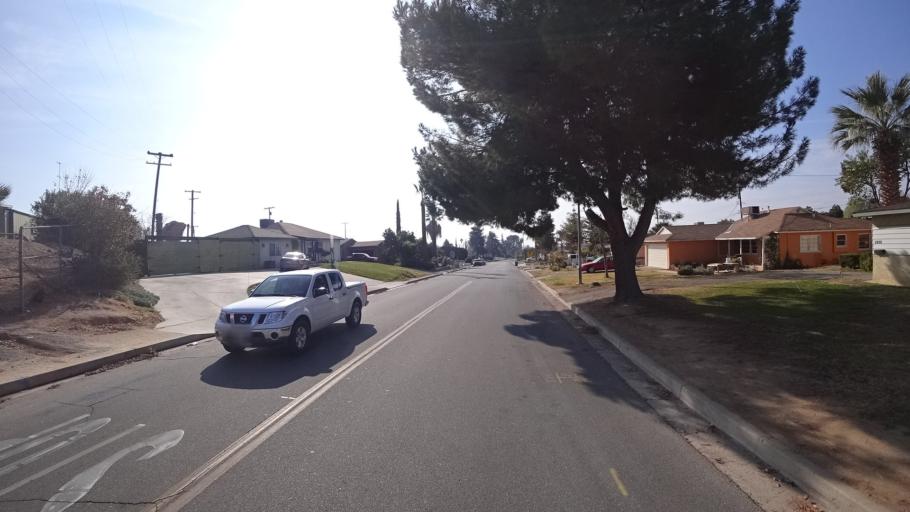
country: US
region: California
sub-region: Kern County
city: Bakersfield
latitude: 35.3897
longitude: -118.9541
